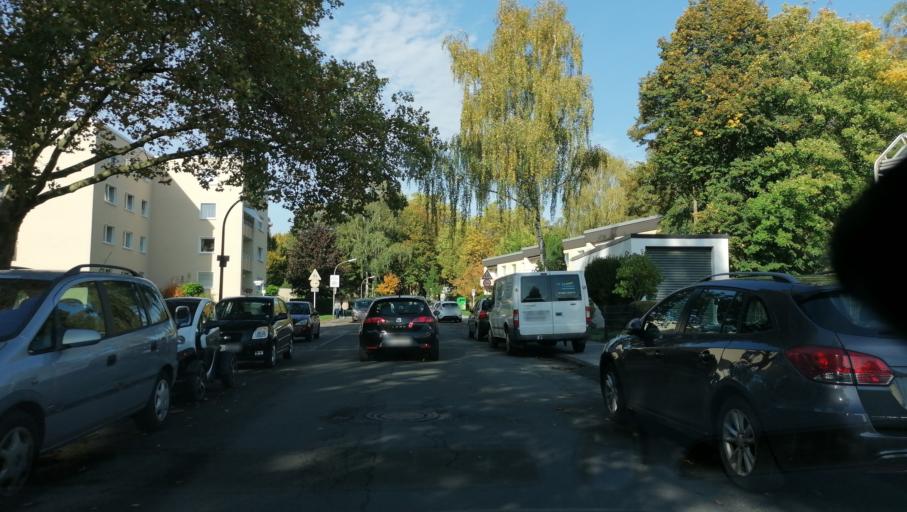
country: DE
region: North Rhine-Westphalia
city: Schwerte
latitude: 51.4979
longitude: 7.5377
